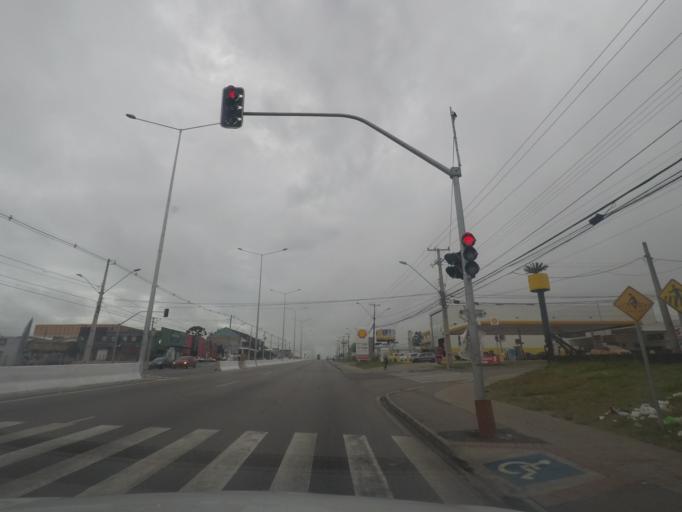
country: BR
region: Parana
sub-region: Pinhais
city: Pinhais
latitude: -25.4328
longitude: -49.1902
